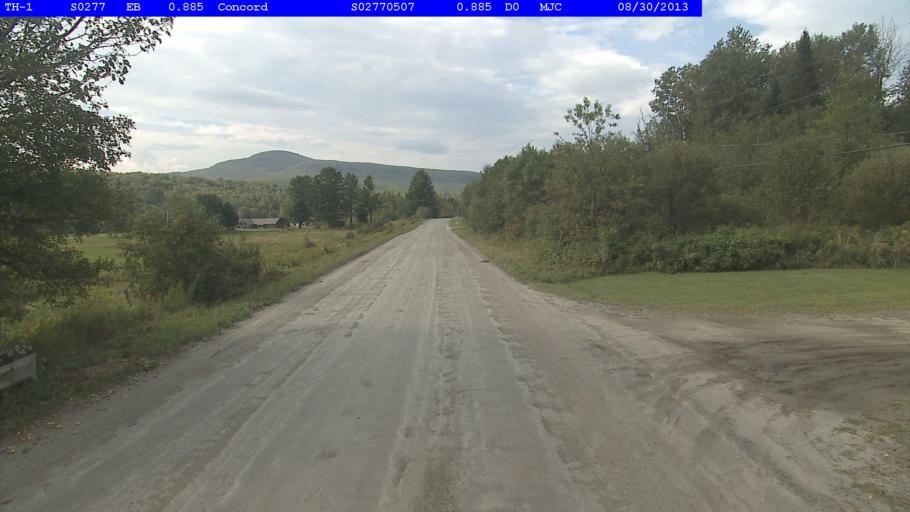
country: US
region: Vermont
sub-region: Caledonia County
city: Lyndonville
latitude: 44.4761
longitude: -71.8628
